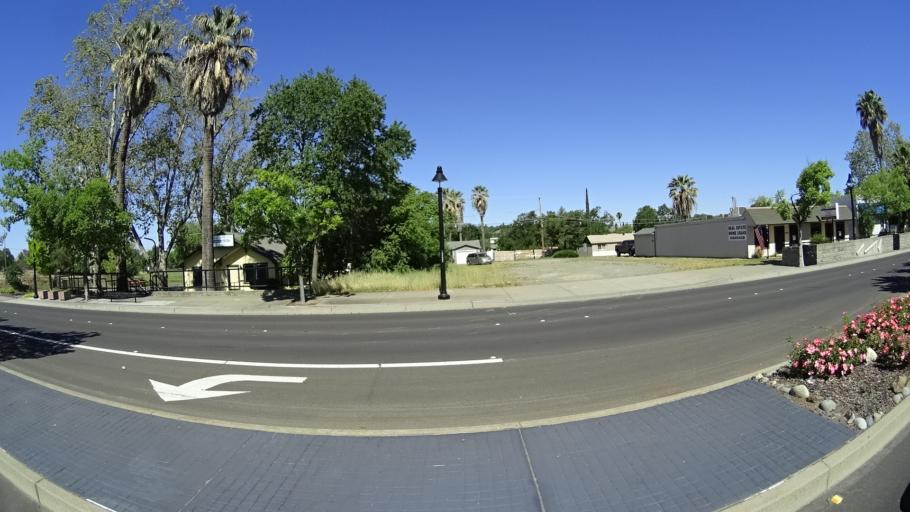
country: US
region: California
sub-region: Placer County
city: Rocklin
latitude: 38.7934
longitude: -121.2340
